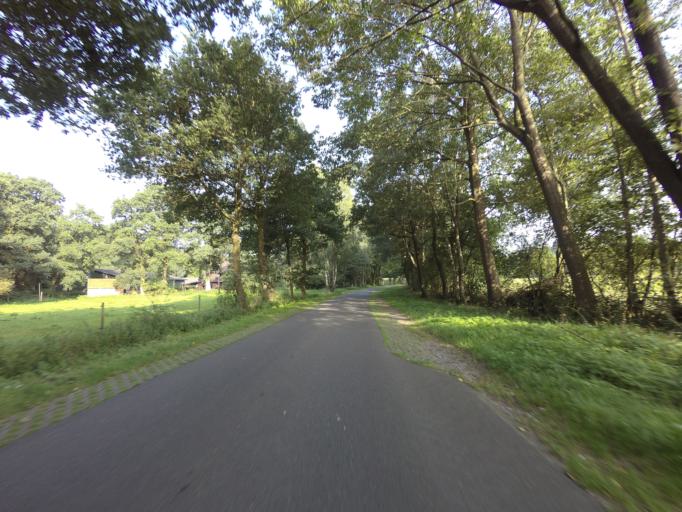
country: DE
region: Lower Saxony
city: Itterbeck
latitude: 52.4923
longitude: 6.8024
